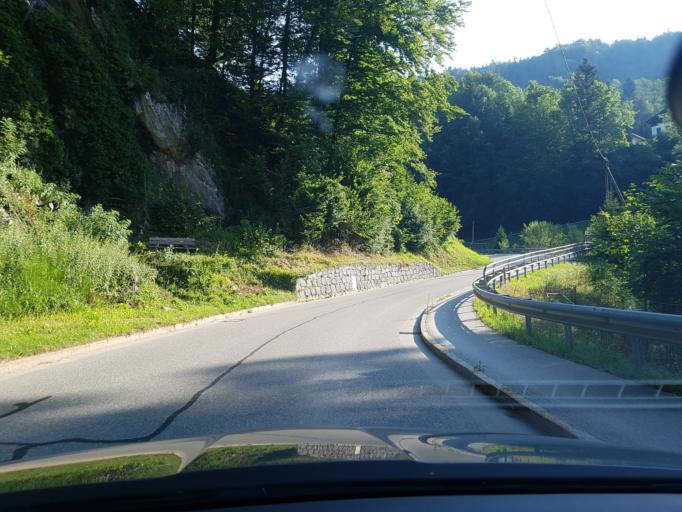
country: DE
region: Bavaria
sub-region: Upper Bavaria
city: Berchtesgaden
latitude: 47.6467
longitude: 13.0024
